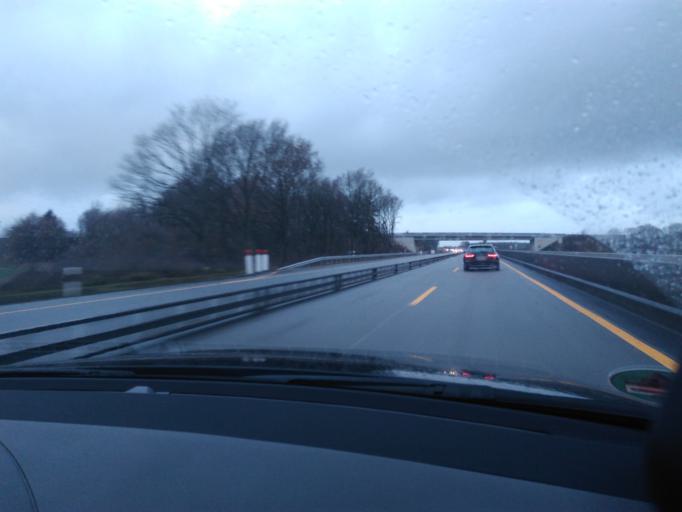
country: DE
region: Schleswig-Holstein
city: Grossenaspe
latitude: 53.9670
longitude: 9.9493
